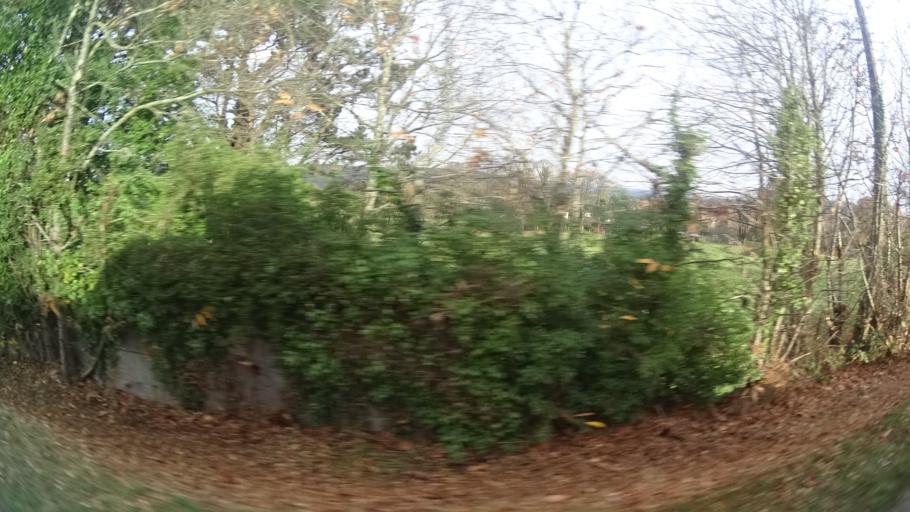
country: FR
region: Pays de la Loire
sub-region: Departement de la Loire-Atlantique
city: Saint-Nicolas-de-Redon
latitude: 47.6460
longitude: -2.0552
